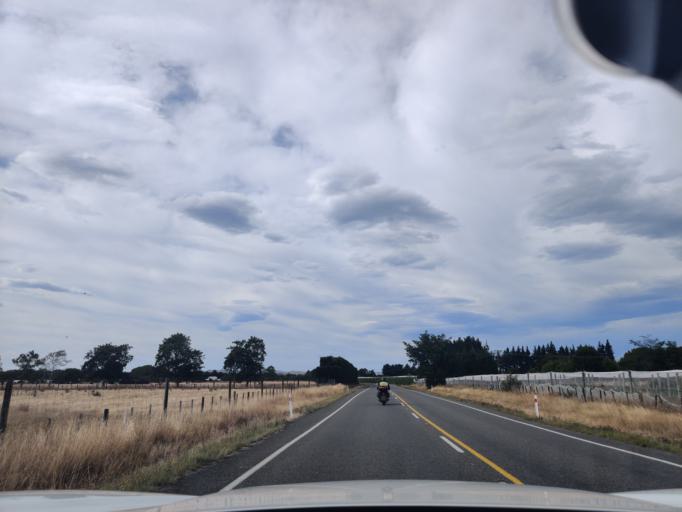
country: NZ
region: Wellington
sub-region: Masterton District
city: Masterton
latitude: -40.8964
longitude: 175.6628
